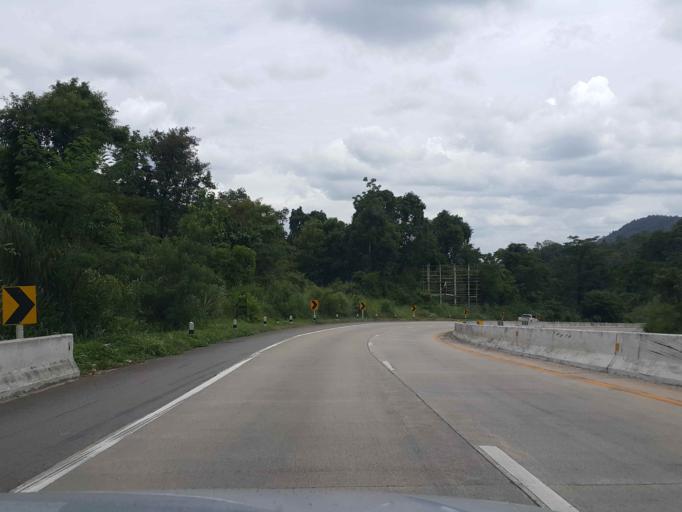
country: TH
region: Lamphun
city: Mae Tha
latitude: 18.4132
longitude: 99.2097
